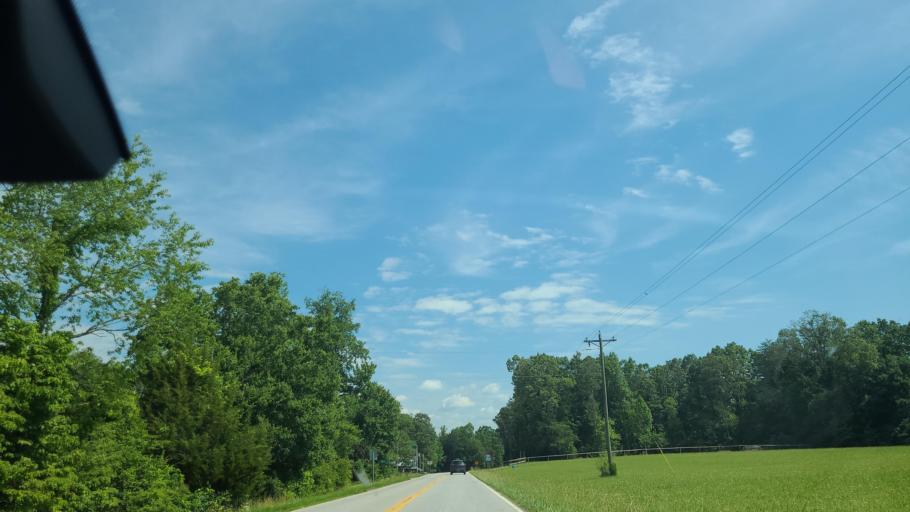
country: US
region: South Carolina
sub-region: Oconee County
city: Walhalla
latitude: 34.8386
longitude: -83.1313
